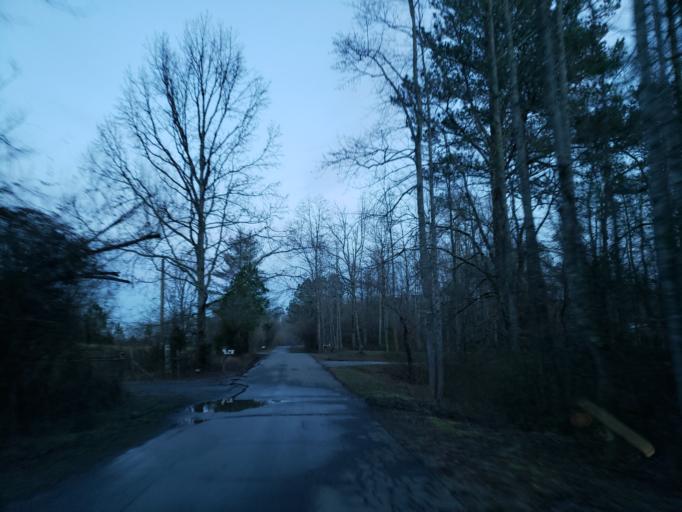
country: US
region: Georgia
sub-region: Cherokee County
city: Ball Ground
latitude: 34.2917
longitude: -84.2981
